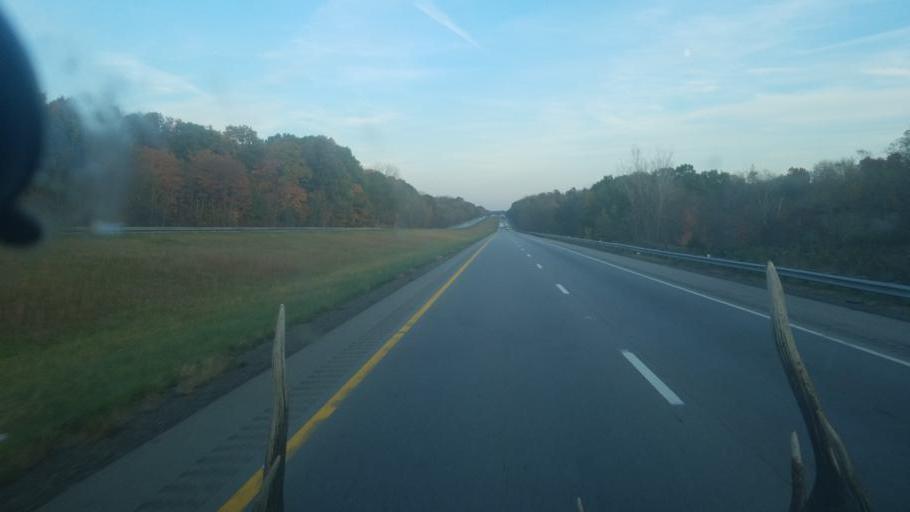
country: US
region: Ohio
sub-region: Muskingum County
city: Zanesville
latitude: 39.9465
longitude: -82.1378
